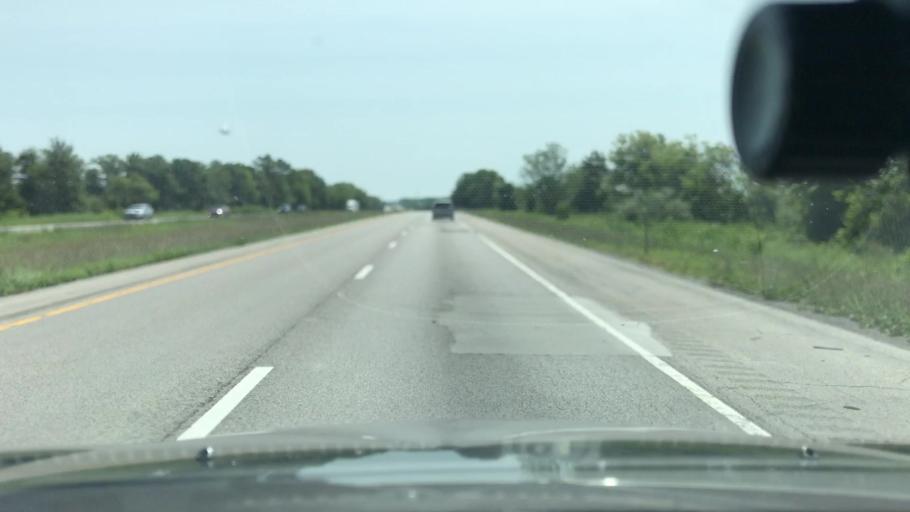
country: US
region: Illinois
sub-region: Jefferson County
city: Mount Vernon
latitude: 38.3506
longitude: -88.9869
